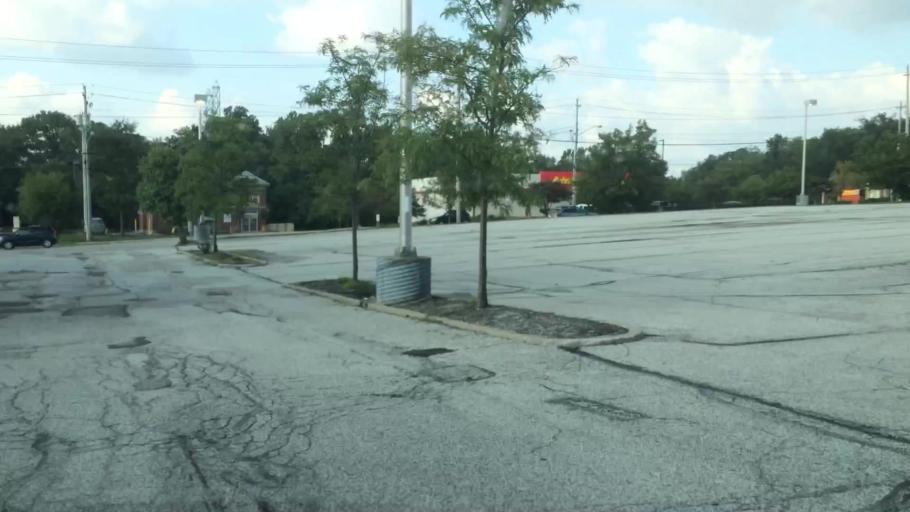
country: US
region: Ohio
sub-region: Cuyahoga County
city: Parma Heights
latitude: 41.3500
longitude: -81.7595
